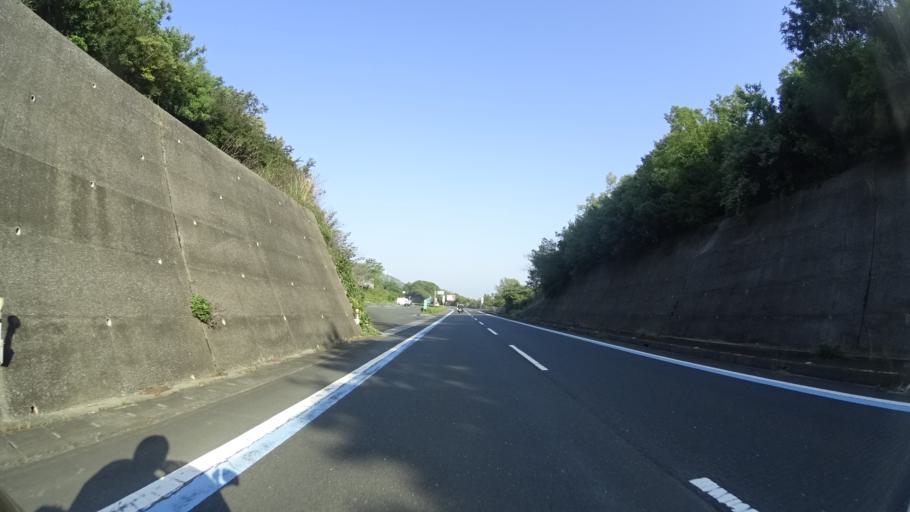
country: JP
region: Ehime
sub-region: Nishiuwa-gun
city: Ikata-cho
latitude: 33.4471
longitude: 132.2600
